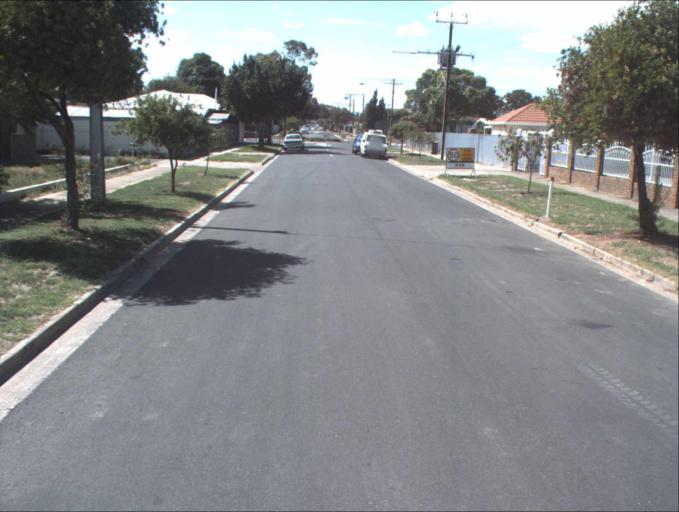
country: AU
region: South Australia
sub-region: Port Adelaide Enfield
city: Blair Athol
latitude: -34.8664
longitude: 138.5855
